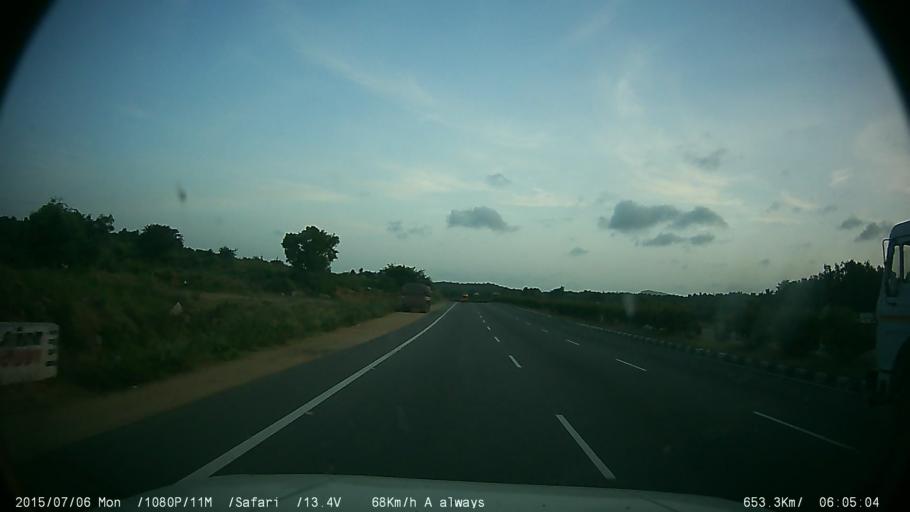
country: IN
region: Tamil Nadu
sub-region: Krishnagiri
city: Krishnagiri
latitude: 12.6198
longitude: 78.0827
